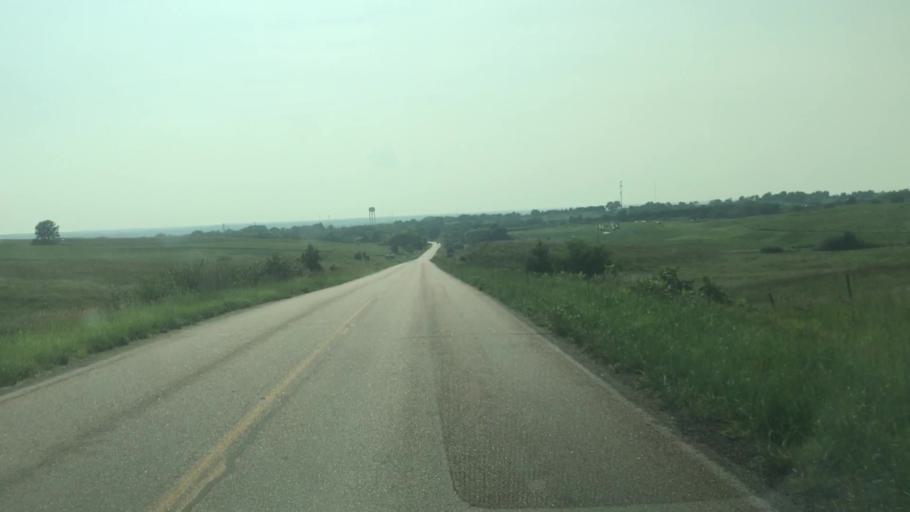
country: US
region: Nebraska
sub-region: Sherman County
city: Loup City
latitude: 41.2793
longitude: -98.9443
